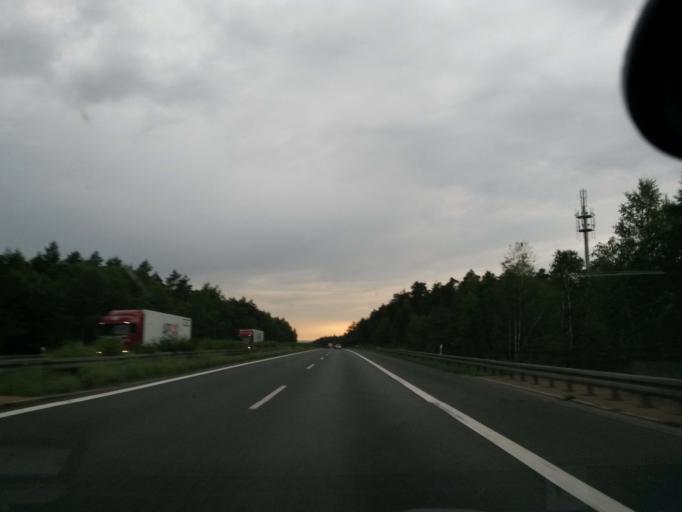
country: DE
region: Bavaria
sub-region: Regierungsbezirk Mittelfranken
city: Schwarzenbruck
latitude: 49.4031
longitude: 11.2566
